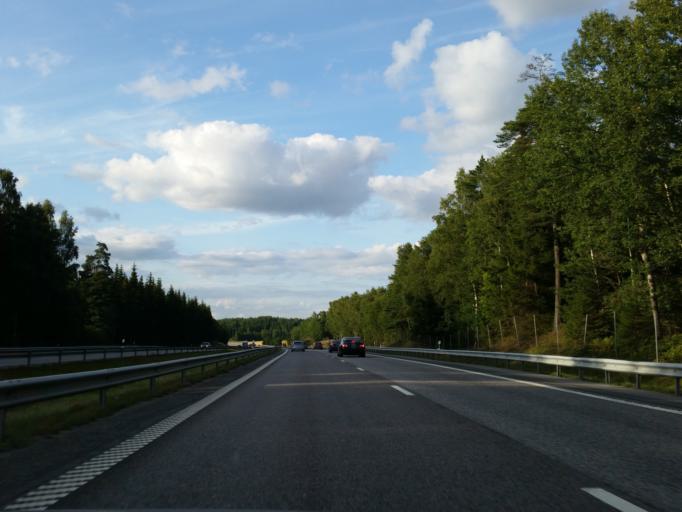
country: SE
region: Stockholm
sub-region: Sodertalje Kommun
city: Pershagen
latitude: 59.0994
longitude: 17.6069
